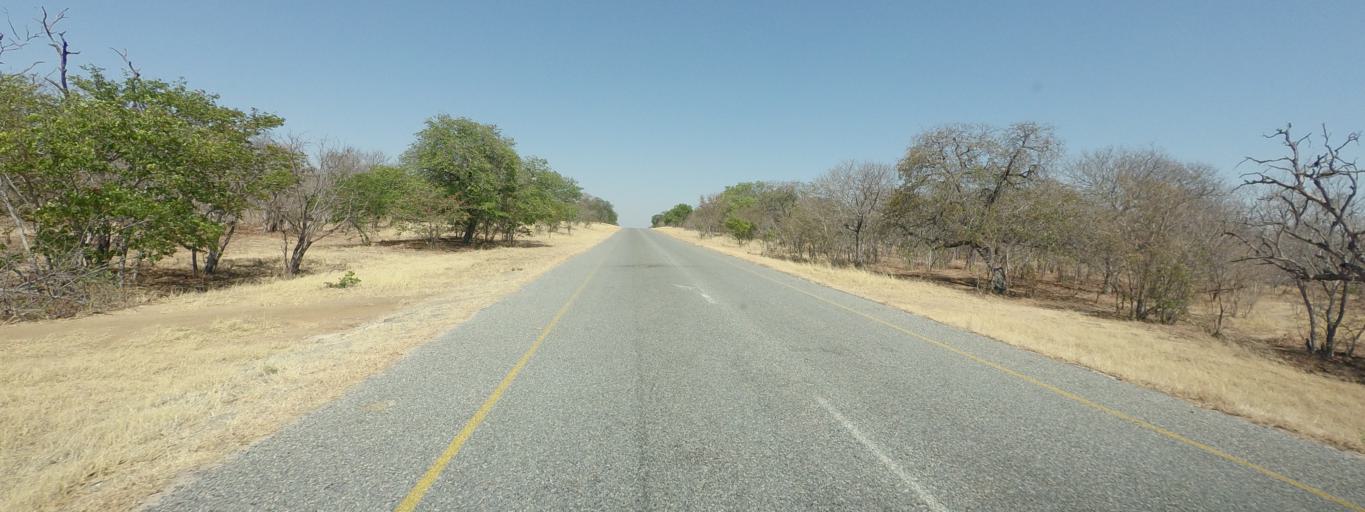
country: BW
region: North West
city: Kasane
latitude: -17.9217
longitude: 25.0154
